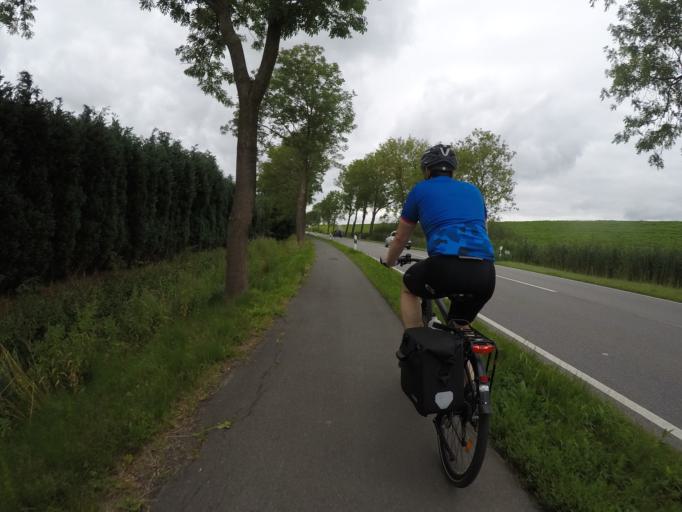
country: DE
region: Lower Saxony
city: Grunendeich
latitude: 53.5834
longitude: 9.5924
